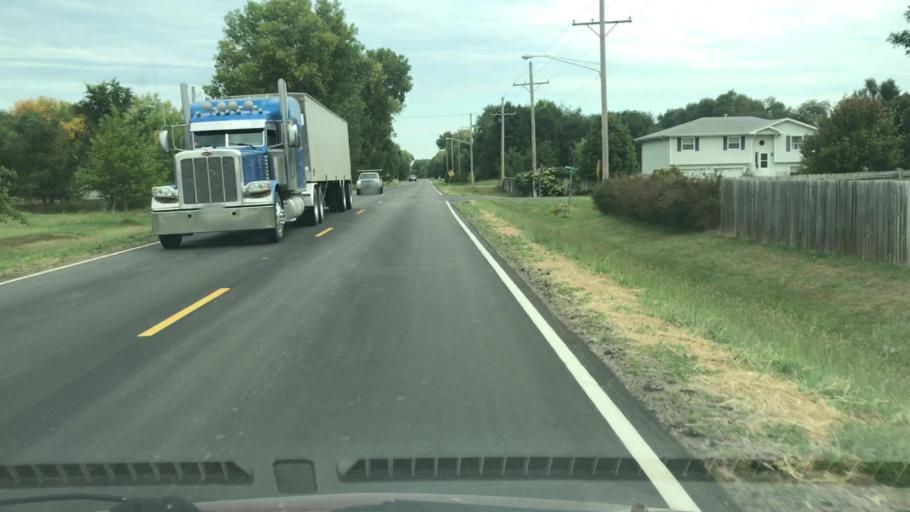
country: US
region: Nebraska
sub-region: Hall County
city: Grand Island
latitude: 40.9185
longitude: -98.3017
